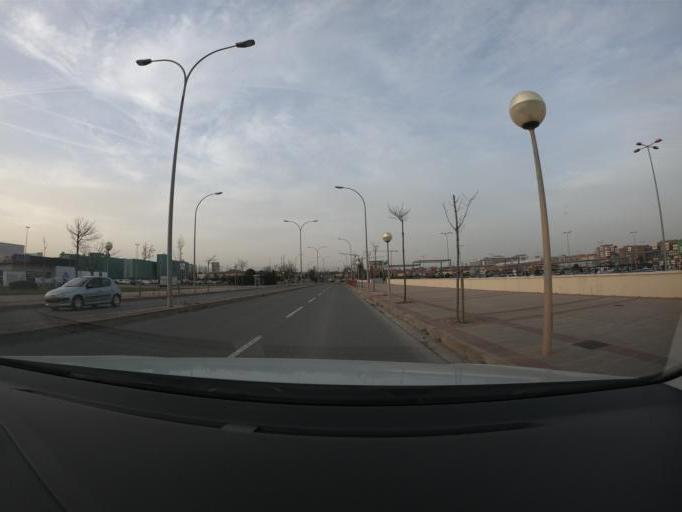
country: ES
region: La Rioja
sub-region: Provincia de La Rioja
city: Logrono
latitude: 42.4521
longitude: -2.4710
